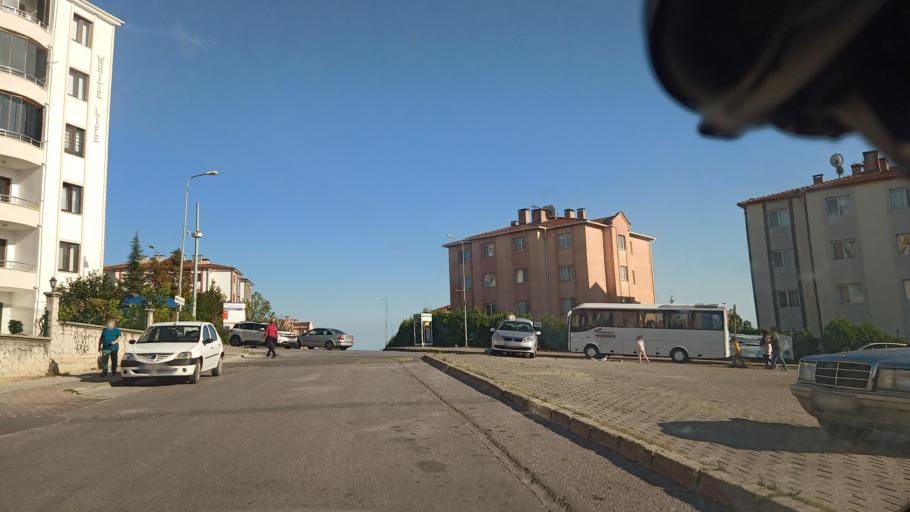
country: TR
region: Sakarya
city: Kazimpasa
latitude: 40.8589
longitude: 30.2894
